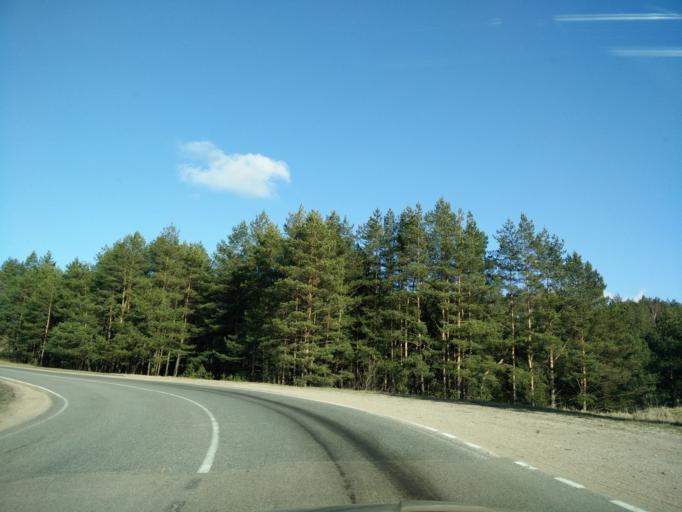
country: LT
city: Vilkija
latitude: 55.0350
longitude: 23.5873
